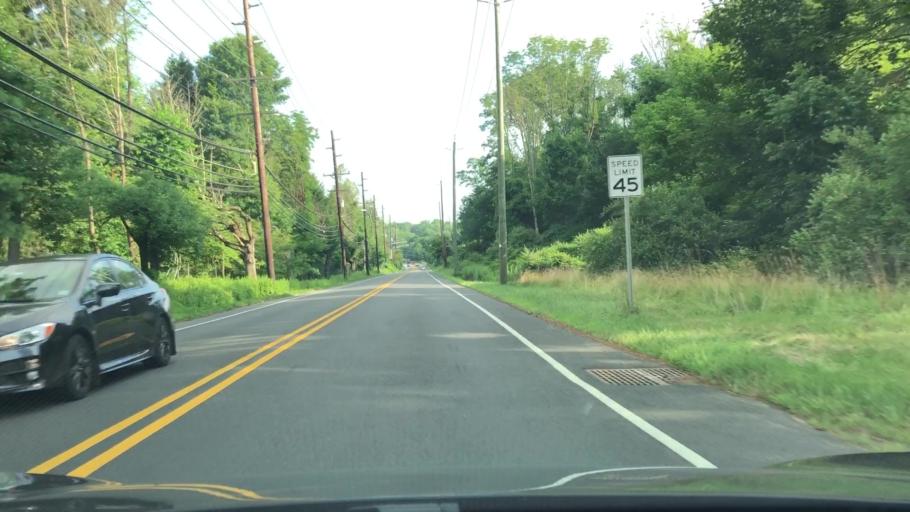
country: US
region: New Jersey
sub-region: Mercer County
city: Lawrenceville
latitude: 40.3391
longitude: -74.7224
